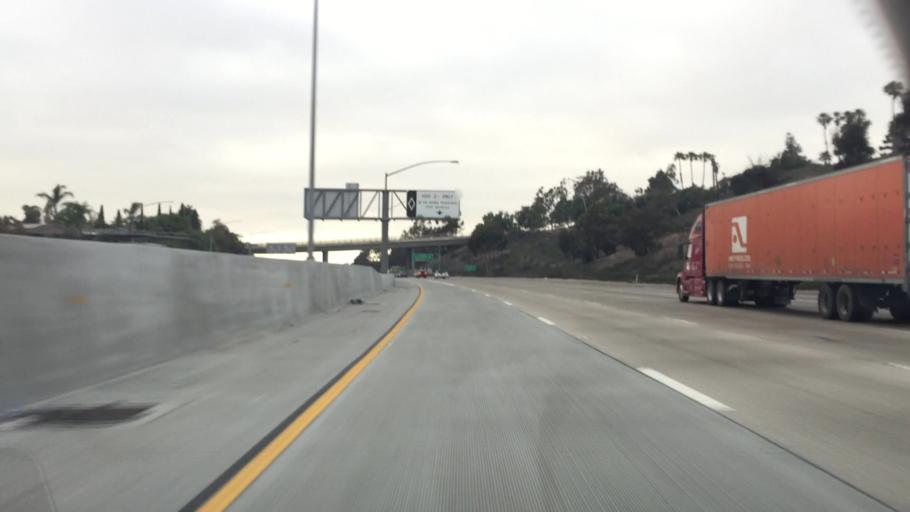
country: US
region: California
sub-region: San Diego County
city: Bonita
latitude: 32.6313
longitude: -117.0448
